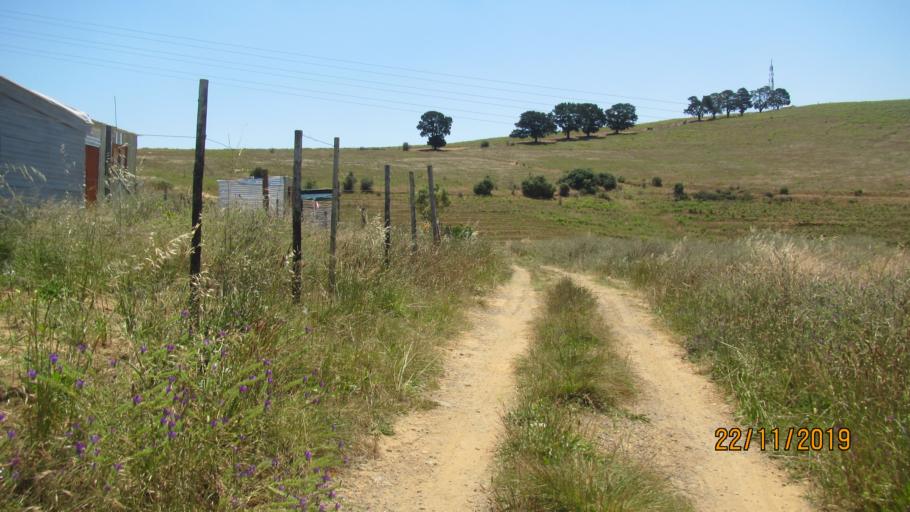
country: ZA
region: Western Cape
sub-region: Cape Winelands District Municipality
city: Stellenbosch
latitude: -33.9201
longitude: 18.8364
